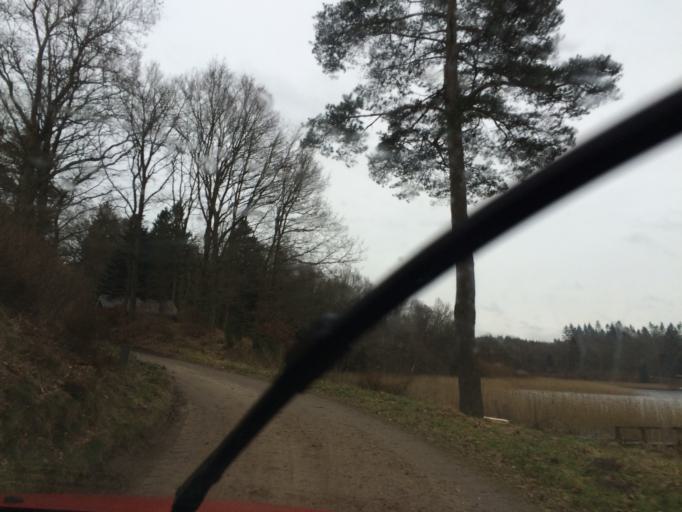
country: DK
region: Central Jutland
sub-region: Silkeborg Kommune
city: Virklund
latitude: 56.0306
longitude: 9.4914
